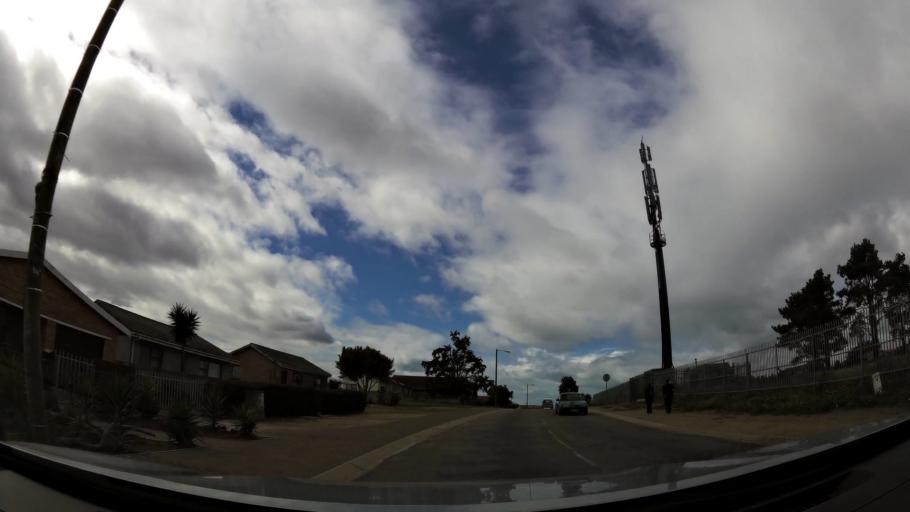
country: ZA
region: Western Cape
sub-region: Eden District Municipality
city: George
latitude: -34.0178
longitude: 22.4679
